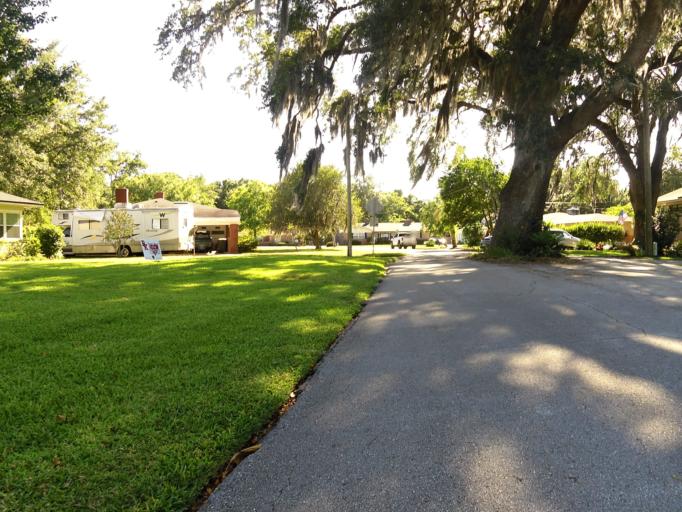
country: US
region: Florida
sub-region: Duval County
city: Jacksonville
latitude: 30.3121
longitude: -81.6162
